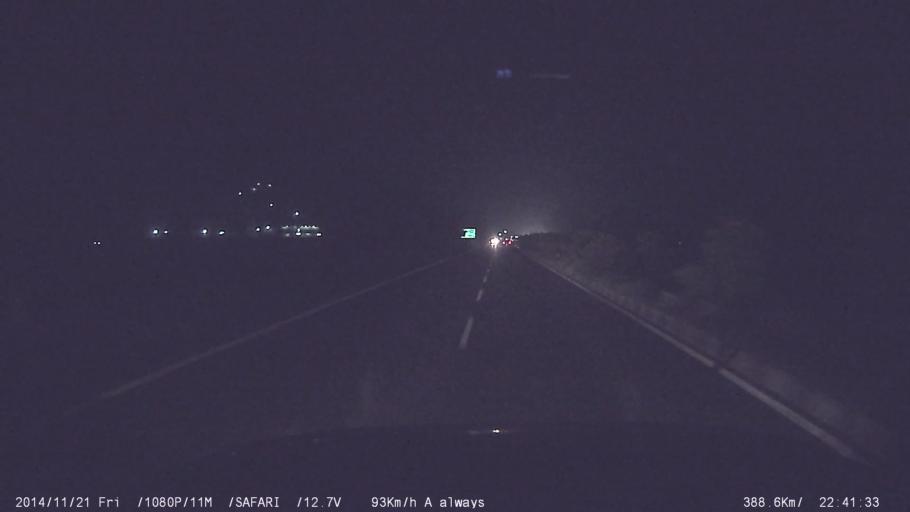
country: IN
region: Tamil Nadu
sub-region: Villupuram
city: Tindivanam
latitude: 12.2482
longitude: 79.6698
